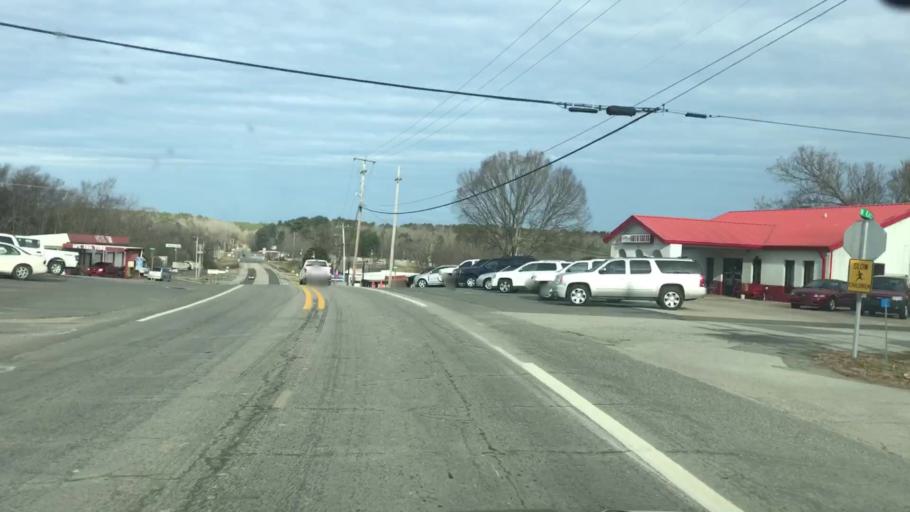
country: US
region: Arkansas
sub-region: Montgomery County
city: Mount Ida
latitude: 34.5579
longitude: -93.6320
